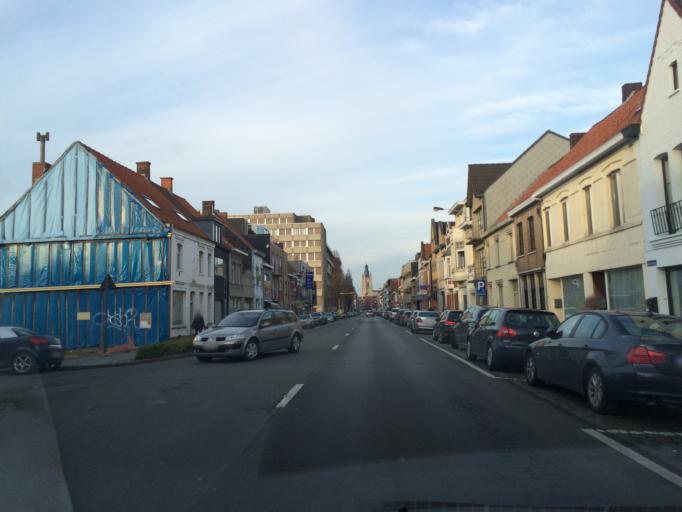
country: BE
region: Flanders
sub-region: Provincie West-Vlaanderen
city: Roeselare
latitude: 50.9377
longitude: 3.1214
